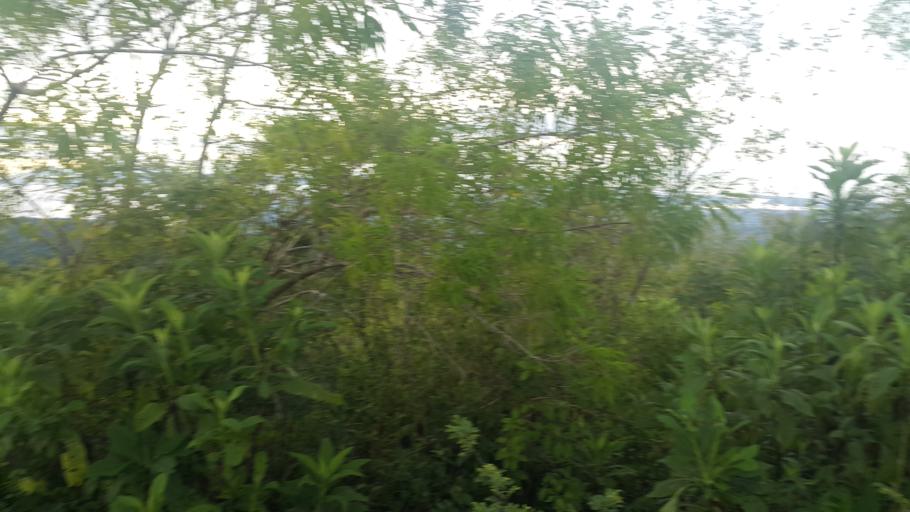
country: NI
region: Chinandega
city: Jiquilillo
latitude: 12.9764
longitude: -87.5587
